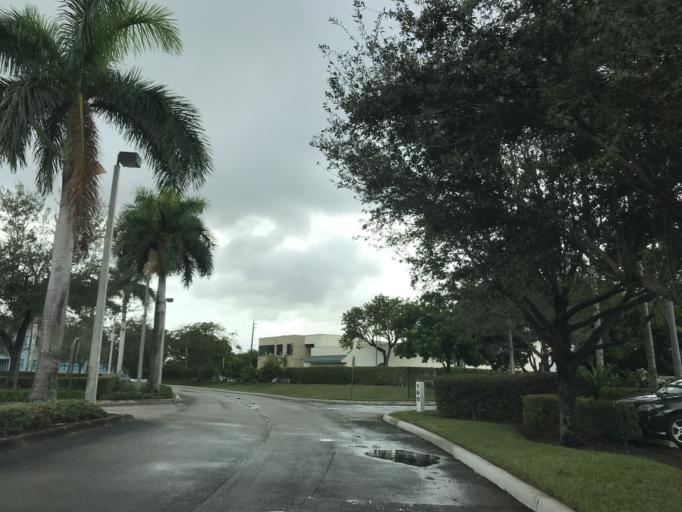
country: US
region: Florida
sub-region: Palm Beach County
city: Delray Beach
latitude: 26.4579
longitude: -80.0946
